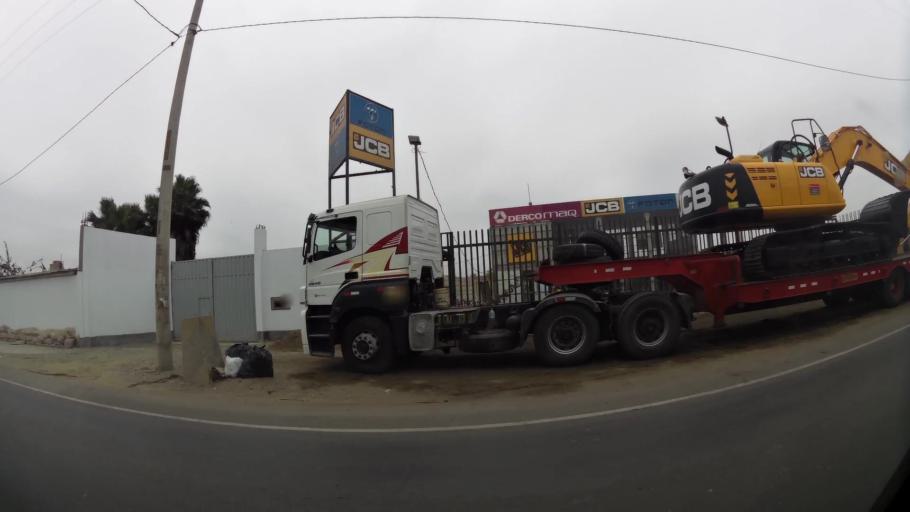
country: PE
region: La Libertad
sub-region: Provincia de Trujillo
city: Buenos Aires
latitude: -8.1395
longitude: -79.0543
